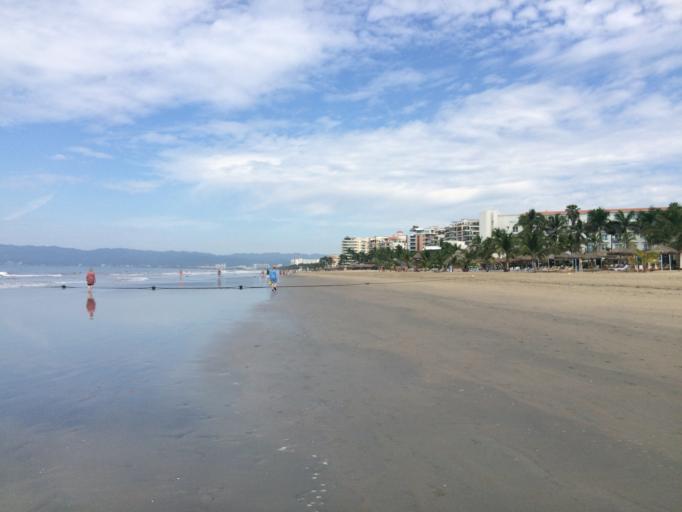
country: MX
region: Nayarit
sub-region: Bahia de Banderas
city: Las Jarretaderas
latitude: 20.6953
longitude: -105.2980
